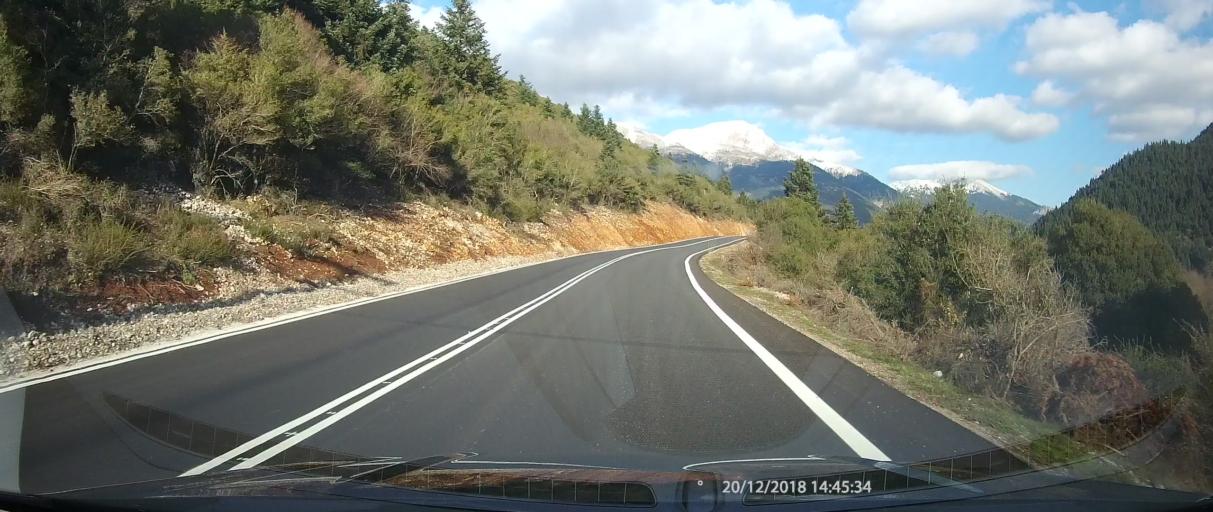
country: GR
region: Central Greece
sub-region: Nomos Evrytanias
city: Karpenisi
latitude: 38.8890
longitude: 21.7611
